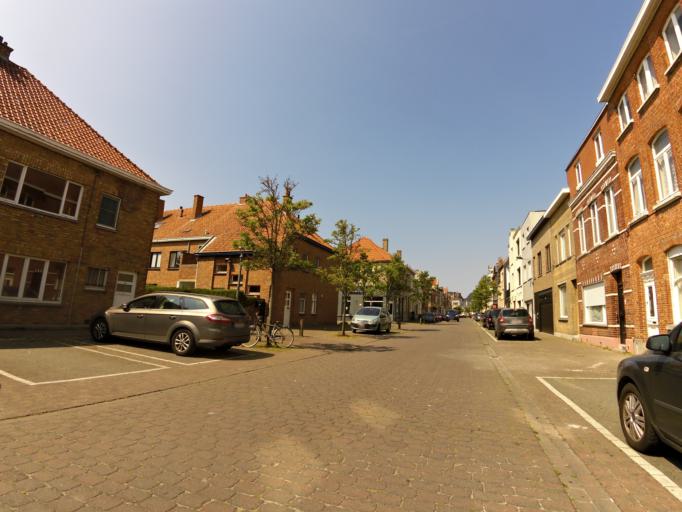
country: BE
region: Flanders
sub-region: Provincie West-Vlaanderen
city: Ostend
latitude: 51.2182
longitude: 2.9001
